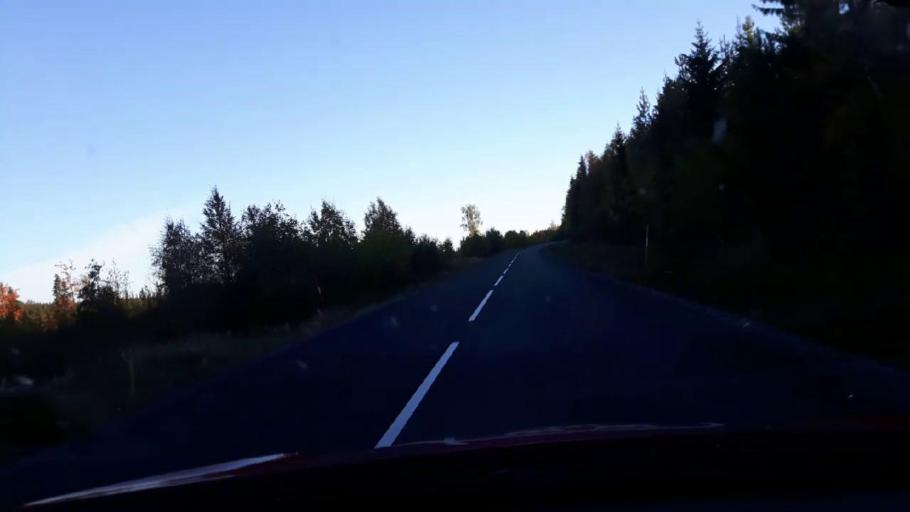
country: SE
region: Jaemtland
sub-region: OEstersunds Kommun
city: Lit
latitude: 63.4799
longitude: 14.8803
